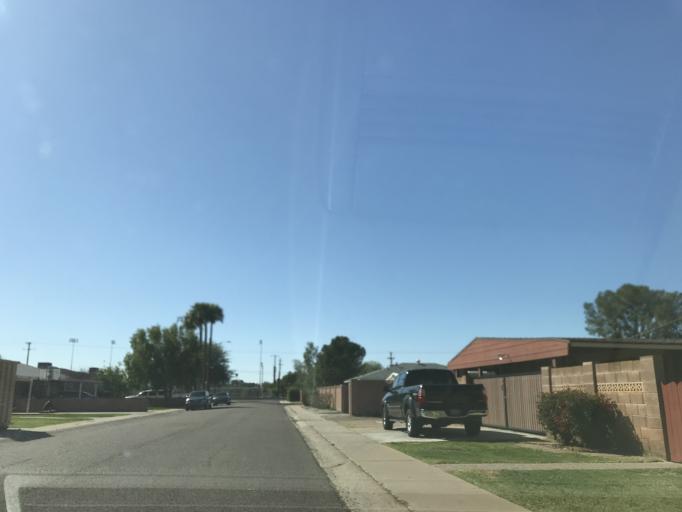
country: US
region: Arizona
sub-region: Maricopa County
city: Phoenix
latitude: 33.5195
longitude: -112.0896
